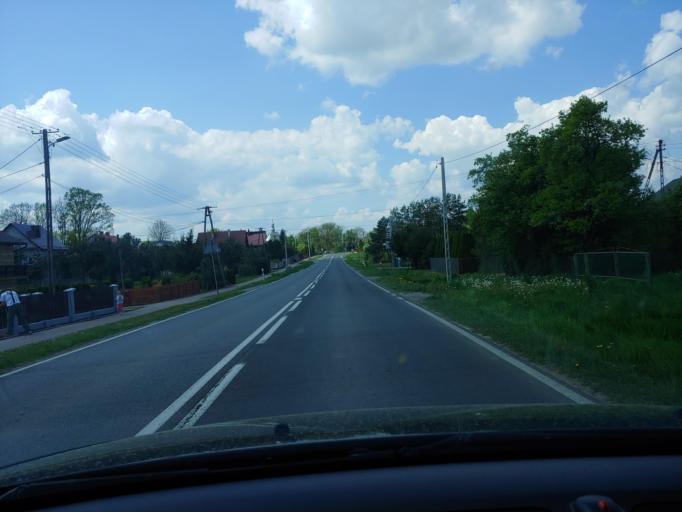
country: PL
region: Subcarpathian Voivodeship
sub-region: Powiat mielecki
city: Wadowice Gorne
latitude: 50.2392
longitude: 21.2943
